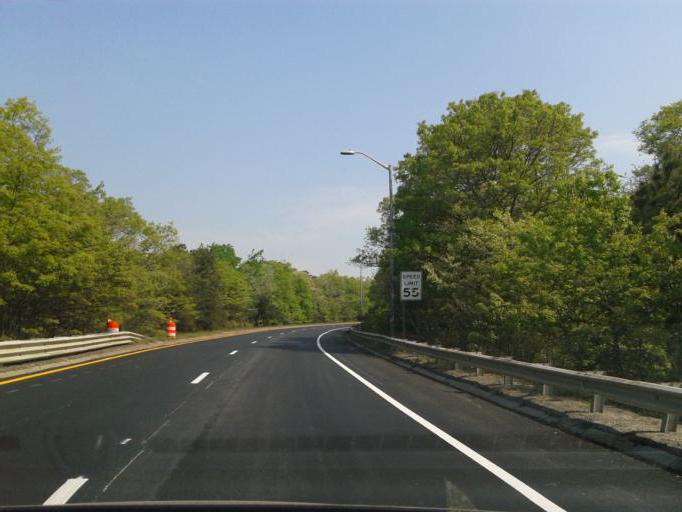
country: US
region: Massachusetts
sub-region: Barnstable County
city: Pocasset
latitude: 41.6865
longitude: -70.5903
